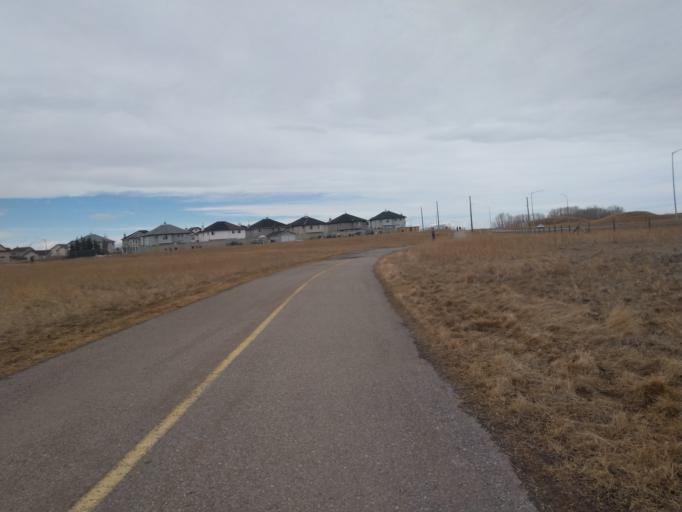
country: CA
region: Alberta
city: Chestermere
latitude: 51.1362
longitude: -113.9273
